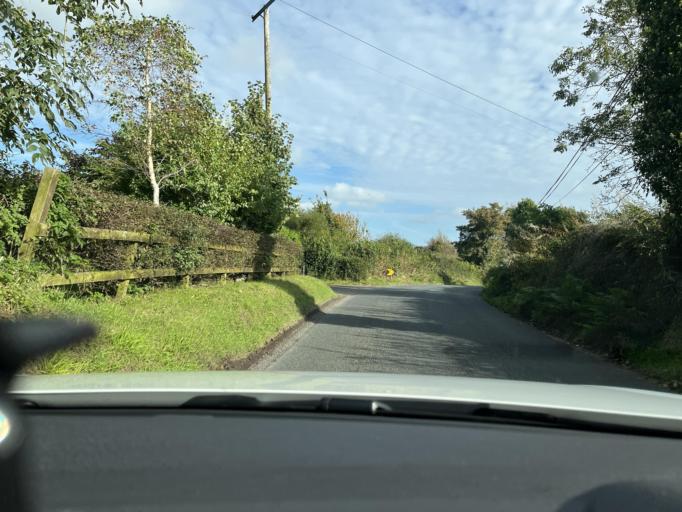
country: IE
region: Connaught
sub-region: Sligo
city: Ballymote
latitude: 54.0841
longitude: -8.4468
